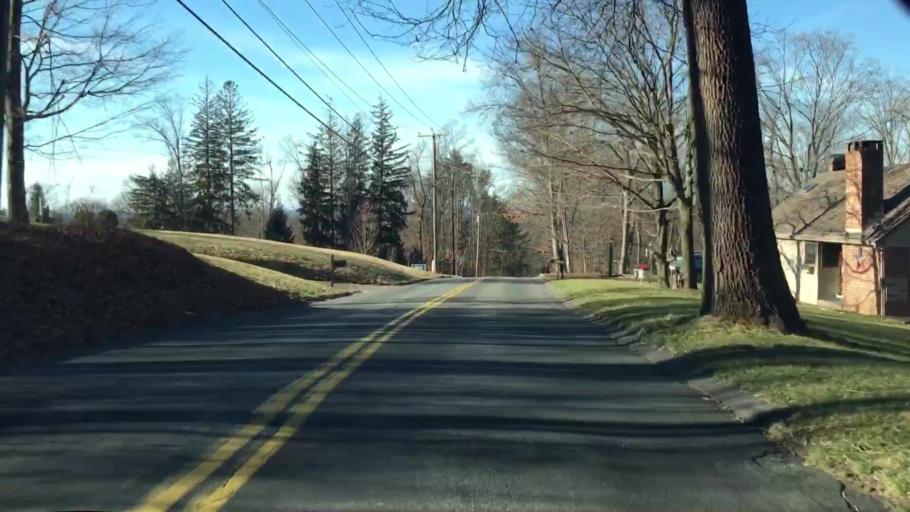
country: US
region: Connecticut
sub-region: Tolland County
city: Somers
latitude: 41.9694
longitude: -72.4354
